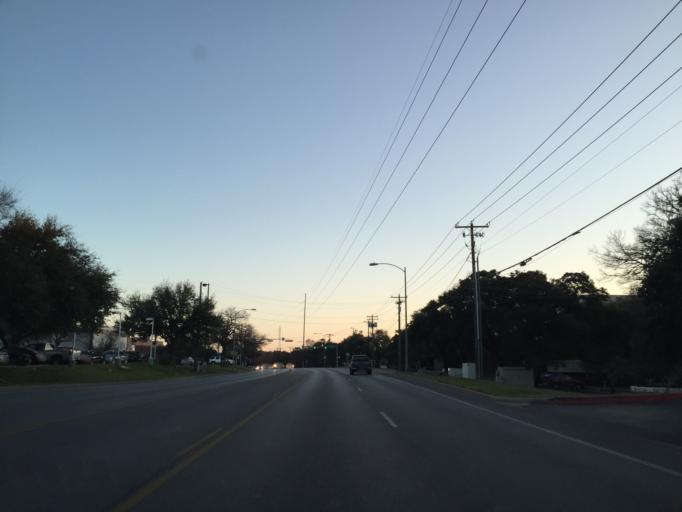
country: US
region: Texas
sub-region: Williamson County
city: Jollyville
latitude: 30.4092
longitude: -97.7477
